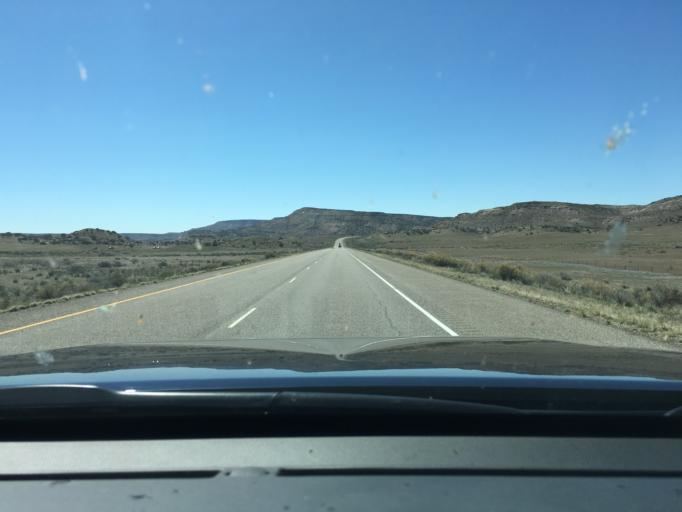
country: US
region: Colorado
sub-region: Mesa County
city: Loma
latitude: 39.1996
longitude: -108.9934
